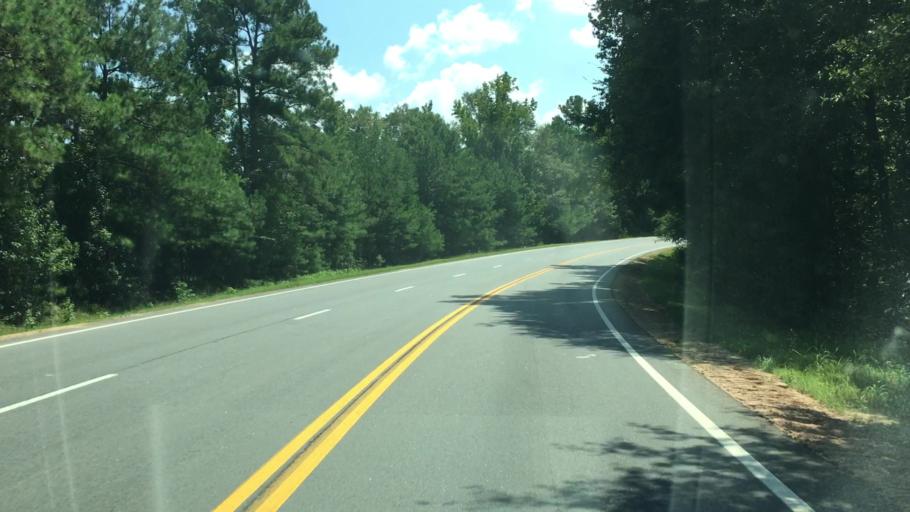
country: US
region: Georgia
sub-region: Morgan County
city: Madison
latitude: 33.7230
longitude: -83.4317
